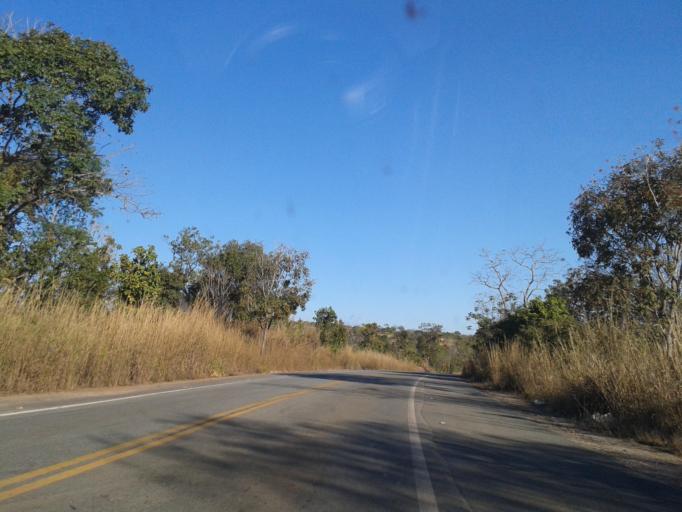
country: BR
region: Goias
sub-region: Itapuranga
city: Itapuranga
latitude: -15.6423
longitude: -50.2250
